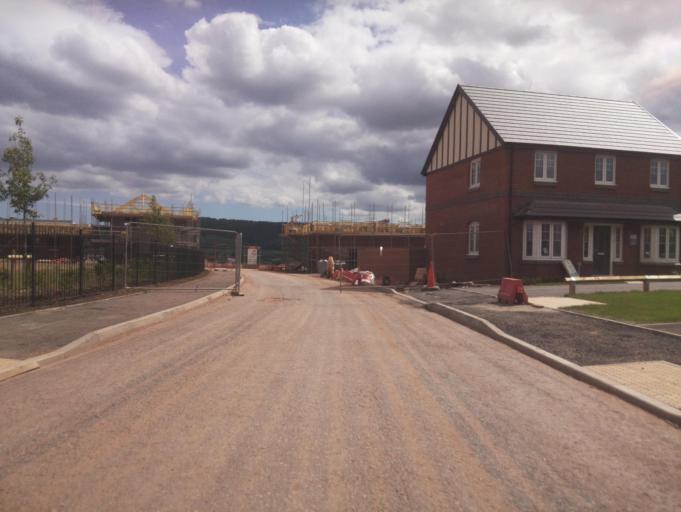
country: GB
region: England
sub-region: Herefordshire
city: Ross on Wye
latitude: 51.9255
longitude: -2.5699
